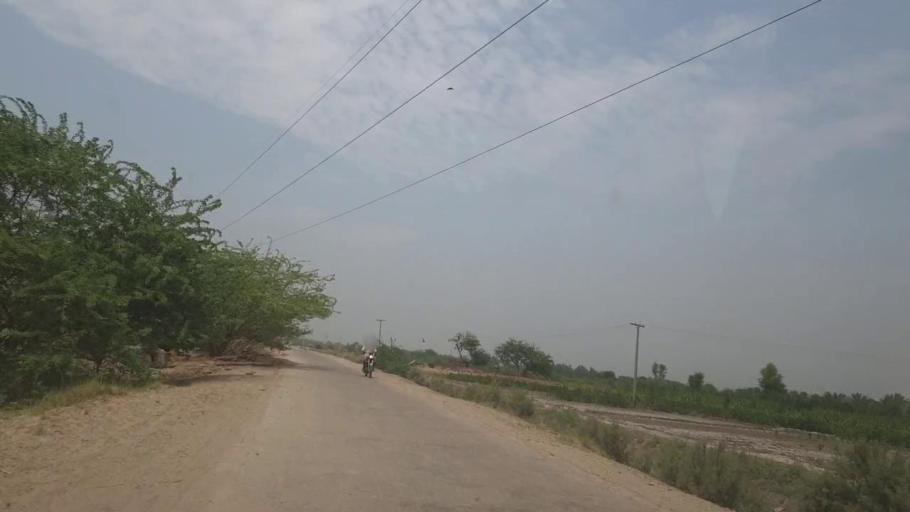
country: PK
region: Sindh
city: Kot Diji
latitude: 27.4341
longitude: 68.7103
